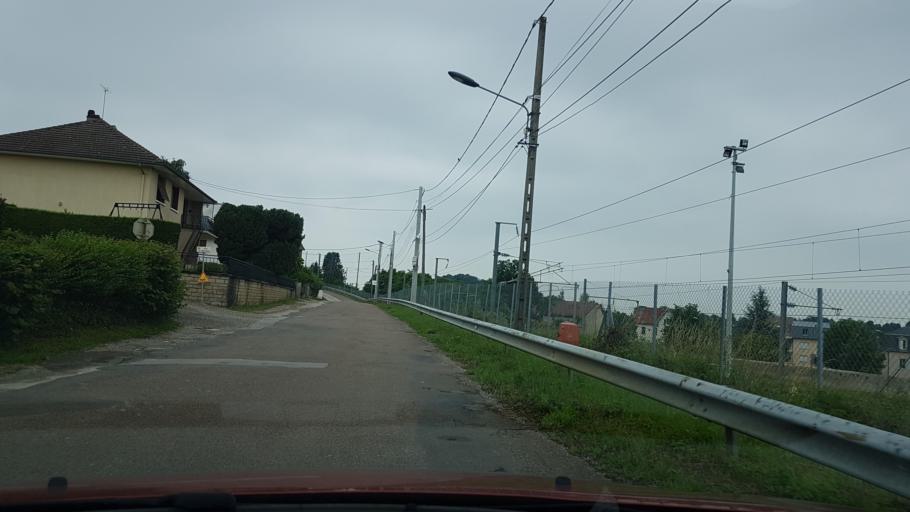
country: FR
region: Franche-Comte
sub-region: Departement du Jura
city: Lons-le-Saunier
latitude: 46.6703
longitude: 5.5415
